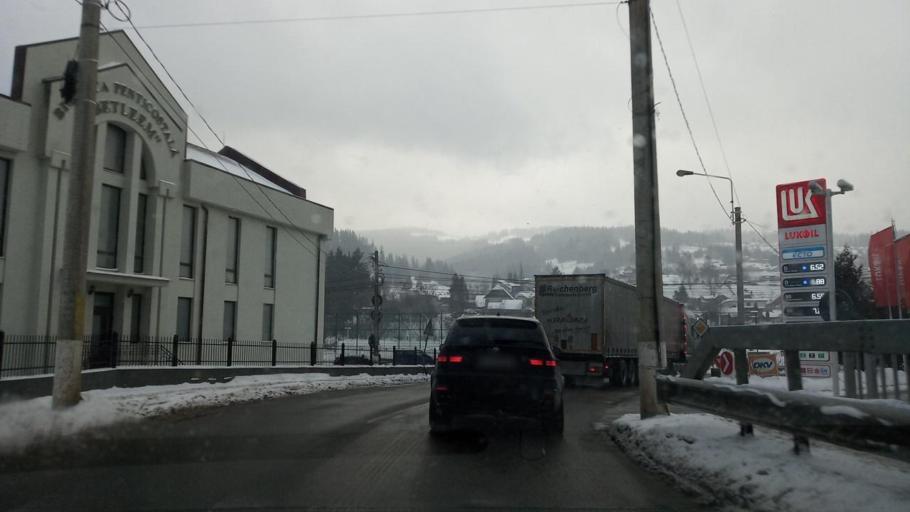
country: RO
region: Suceava
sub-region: Municipiul Vatra Dornei
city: Vatra Dornei
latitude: 47.3465
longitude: 25.3477
